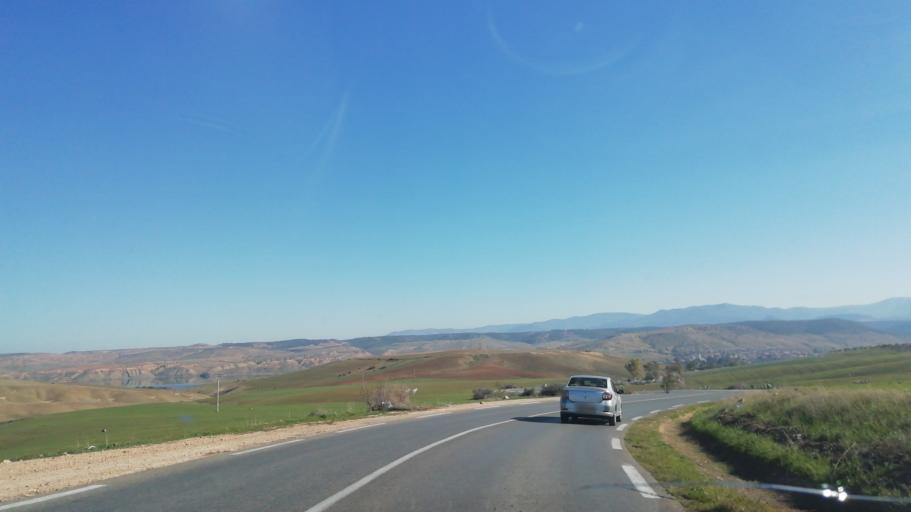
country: DZ
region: Tlemcen
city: Nedroma
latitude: 34.8316
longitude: -1.6721
